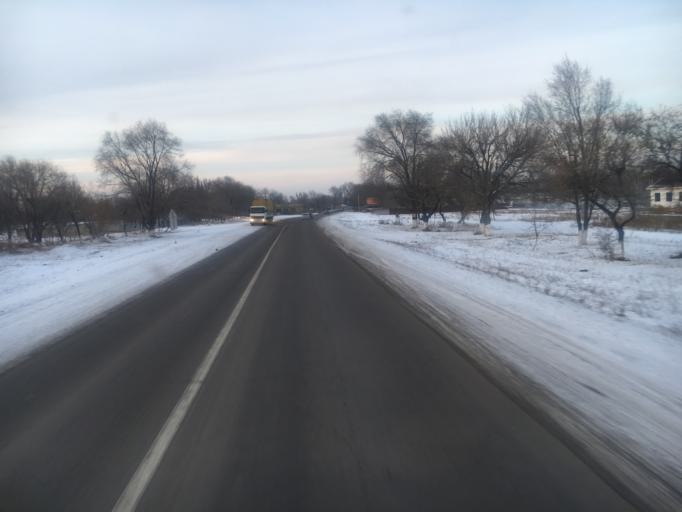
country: KZ
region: Almaty Oblysy
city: Burunday
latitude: 43.3638
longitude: 76.6423
